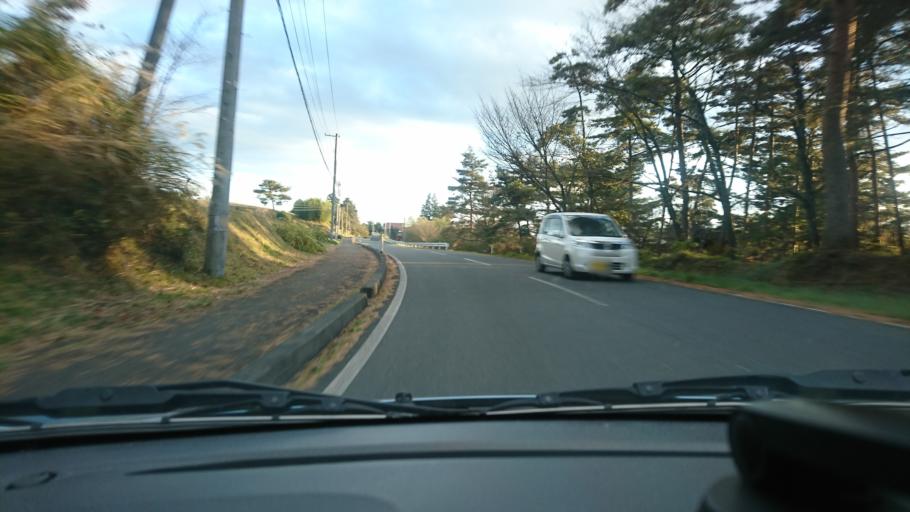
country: JP
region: Iwate
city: Ichinoseki
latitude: 38.8028
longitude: 141.1924
